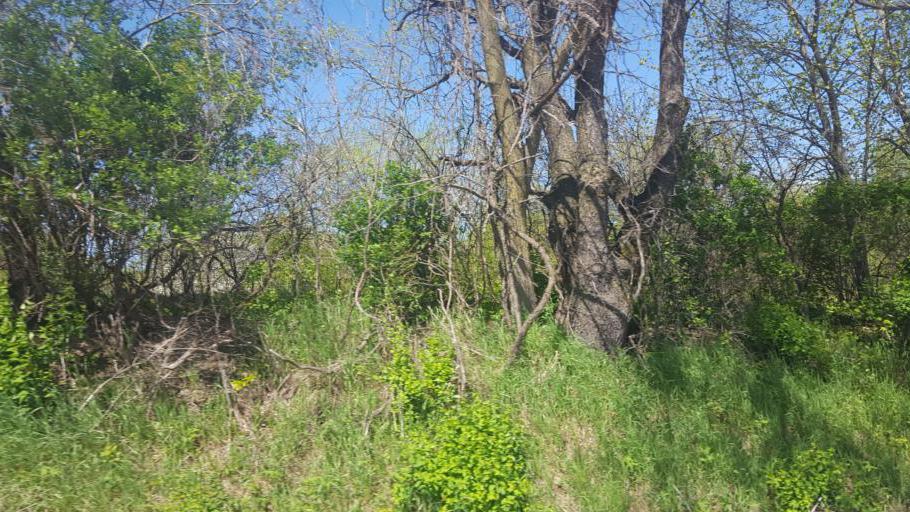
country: US
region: Wisconsin
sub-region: Vernon County
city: Hillsboro
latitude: 43.6368
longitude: -90.3702
